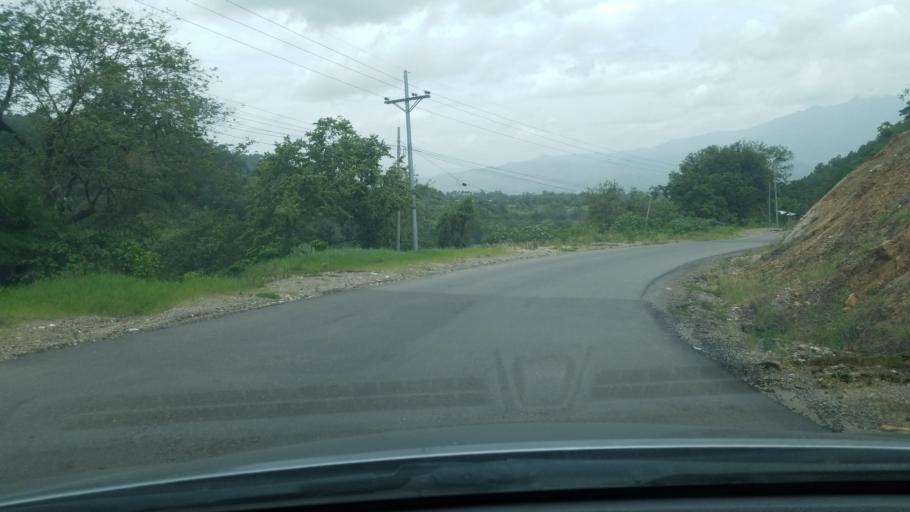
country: HN
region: Copan
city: Ojos de Agua
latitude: 14.6738
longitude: -88.8308
